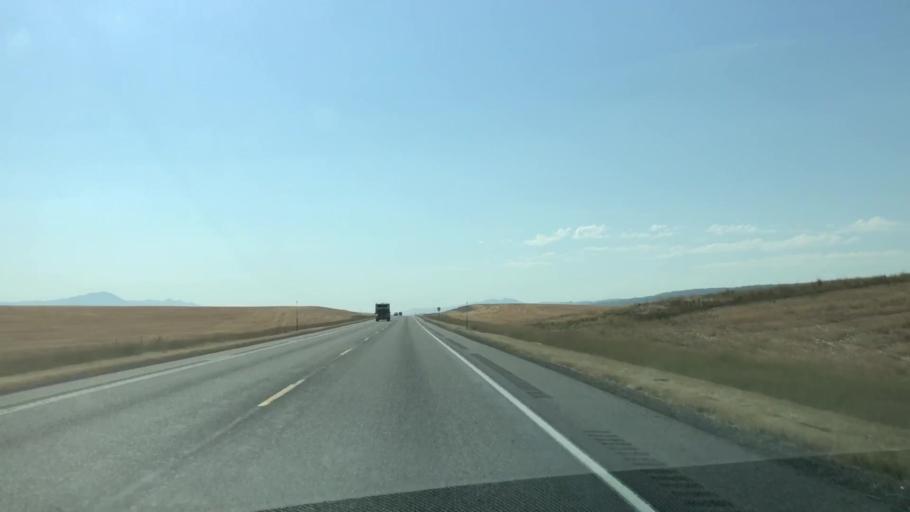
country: US
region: Idaho
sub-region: Madison County
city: Rexburg
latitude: 43.5583
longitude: -111.5404
